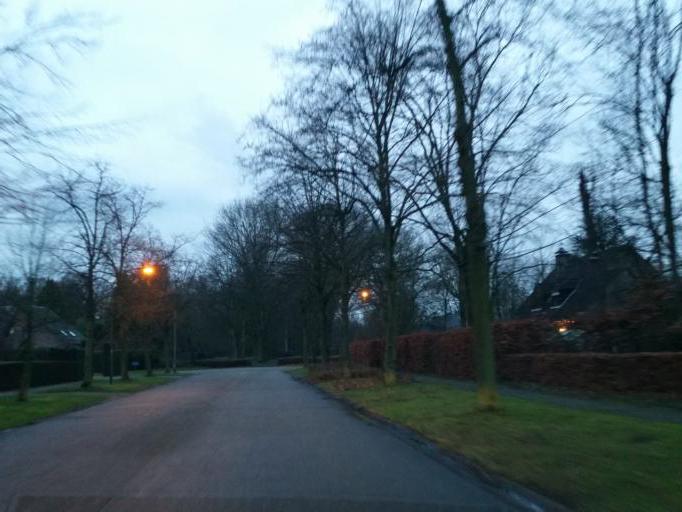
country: BE
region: Flanders
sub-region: Provincie Antwerpen
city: Brasschaat
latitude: 51.3068
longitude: 4.5019
